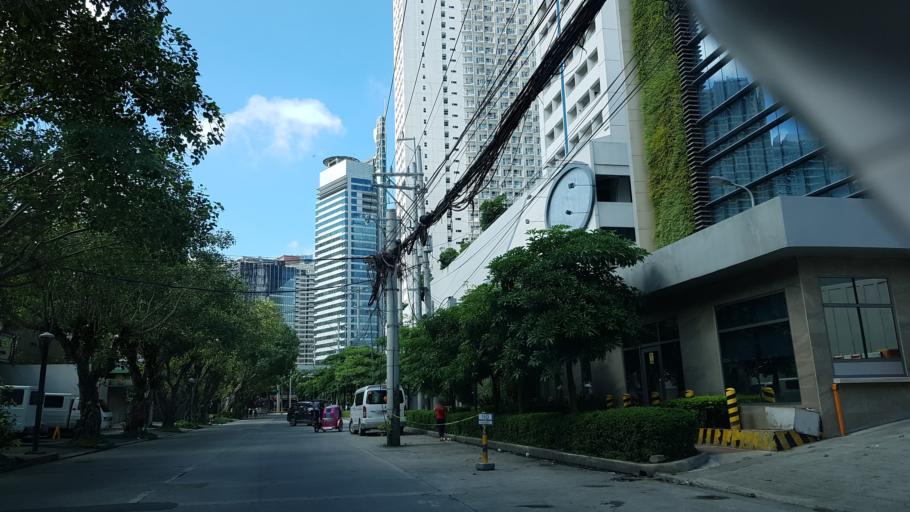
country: PH
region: Metro Manila
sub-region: Makati City
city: Makati City
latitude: 14.5648
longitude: 121.0228
